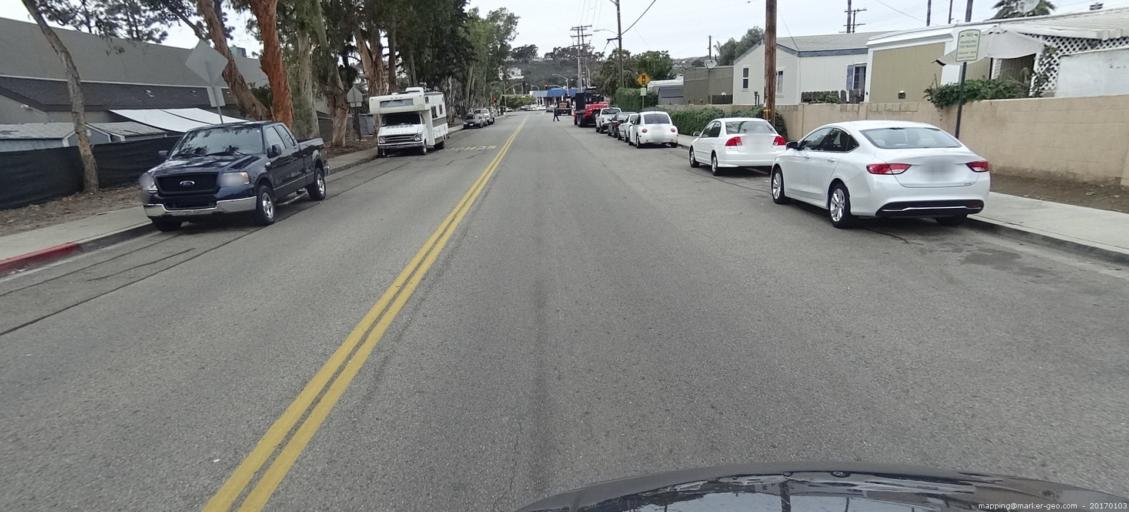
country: US
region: California
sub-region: Orange County
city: Dana Point
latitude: 33.4655
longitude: -117.6756
